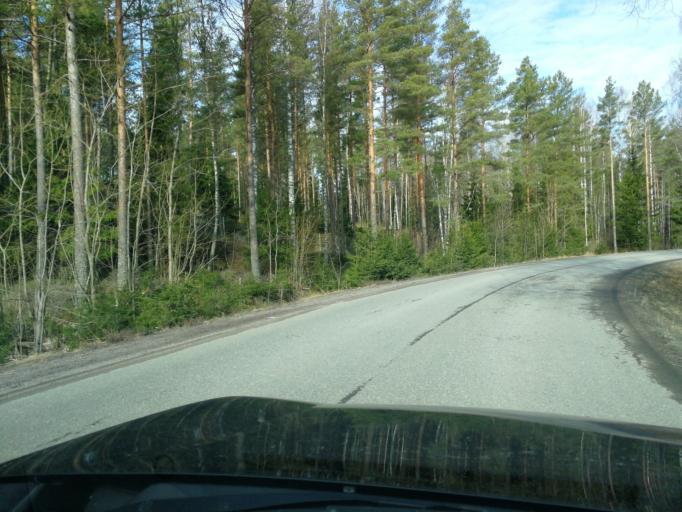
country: FI
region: Uusimaa
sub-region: Helsinki
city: Kirkkonummi
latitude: 60.0913
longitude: 24.3690
